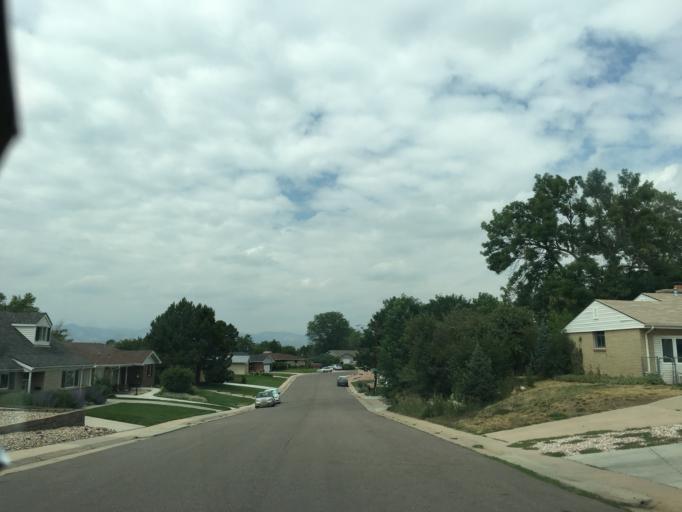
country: US
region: Colorado
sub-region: Arapahoe County
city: Sheridan
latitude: 39.6643
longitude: -105.0354
